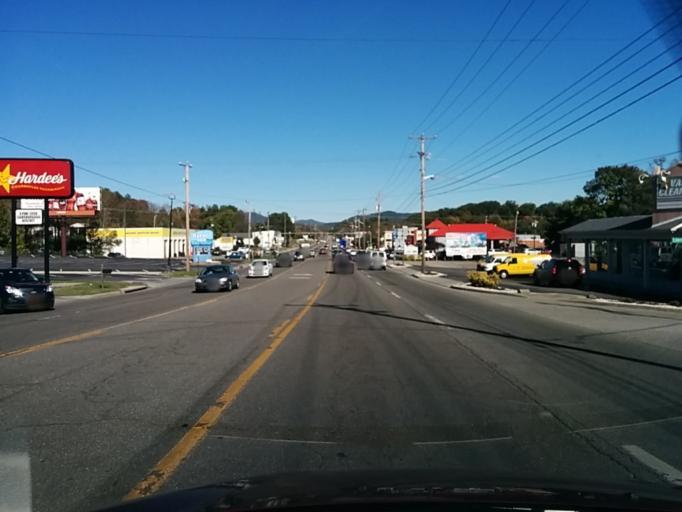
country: US
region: Virginia
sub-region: Roanoke County
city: Hollins
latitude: 37.3474
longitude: -79.9528
